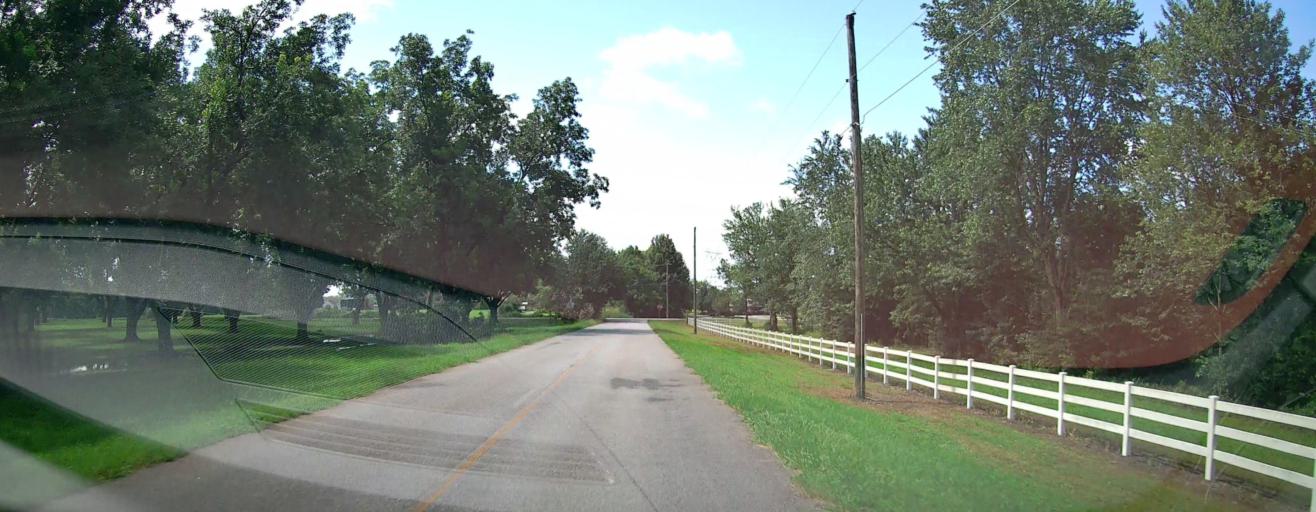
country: US
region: Georgia
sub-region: Peach County
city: Byron
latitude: 32.6530
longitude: -83.7813
